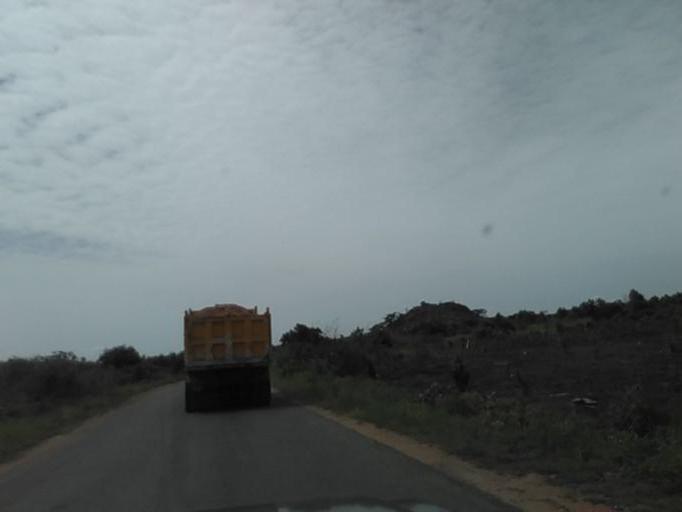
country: GH
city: Akropong
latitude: 6.0951
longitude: 0.0598
